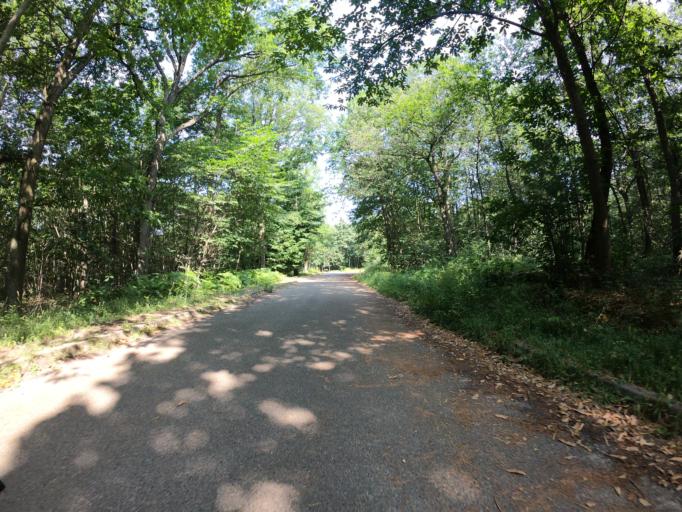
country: FR
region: Ile-de-France
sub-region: Departement de l'Essonne
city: Igny
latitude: 48.7540
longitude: 2.2339
